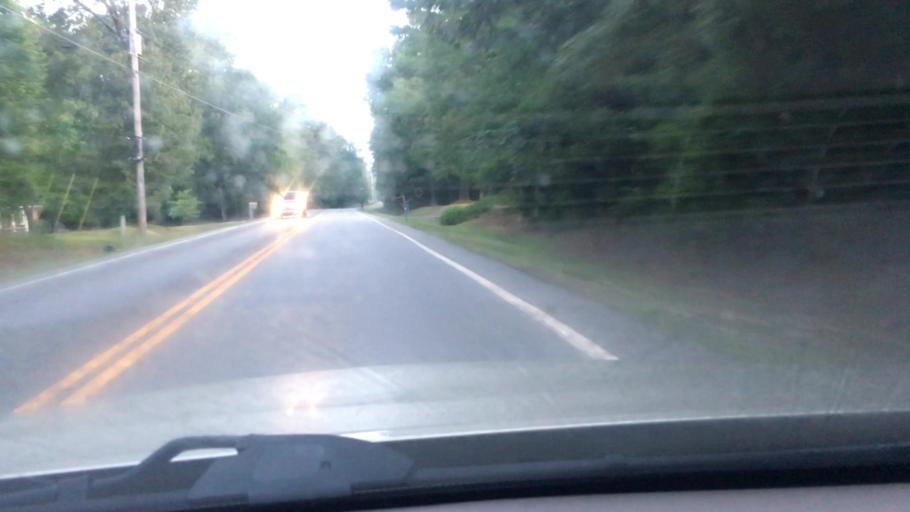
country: US
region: South Carolina
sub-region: Lexington County
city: Irmo
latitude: 34.1420
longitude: -81.1901
